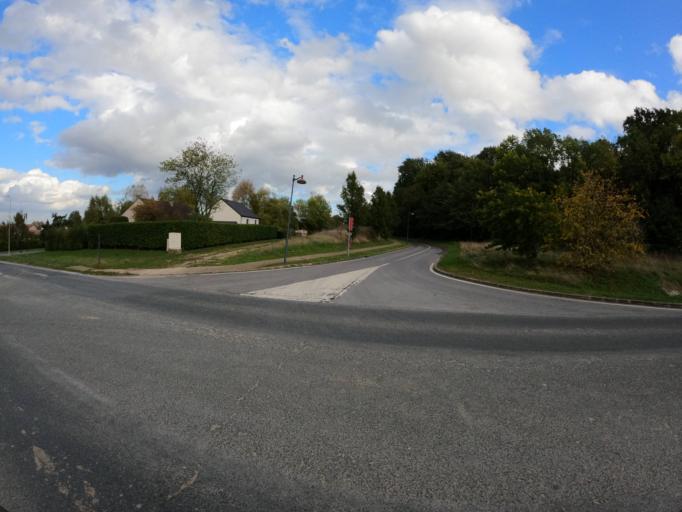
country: FR
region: Ile-de-France
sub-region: Departement de Seine-et-Marne
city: Coupvray
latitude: 48.8875
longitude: 2.8072
